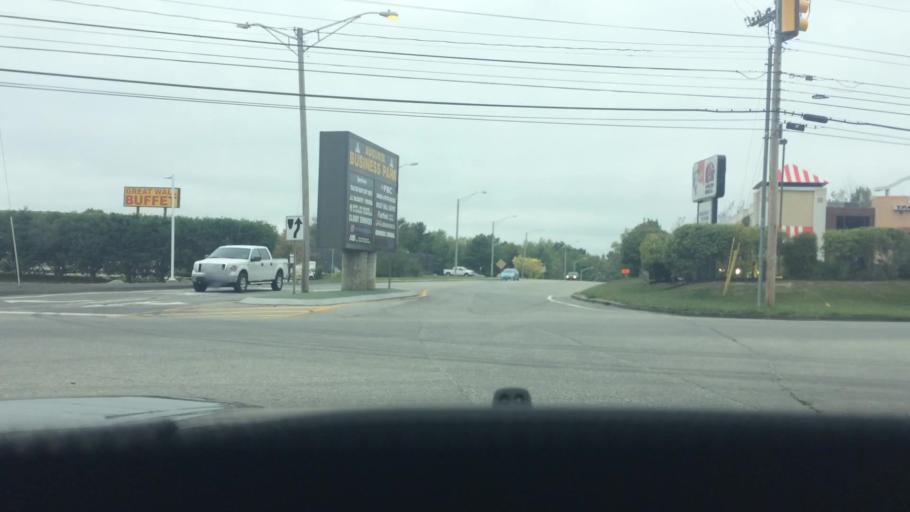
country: US
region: Maine
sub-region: Kennebec County
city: Augusta
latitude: 44.3497
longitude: -69.7963
